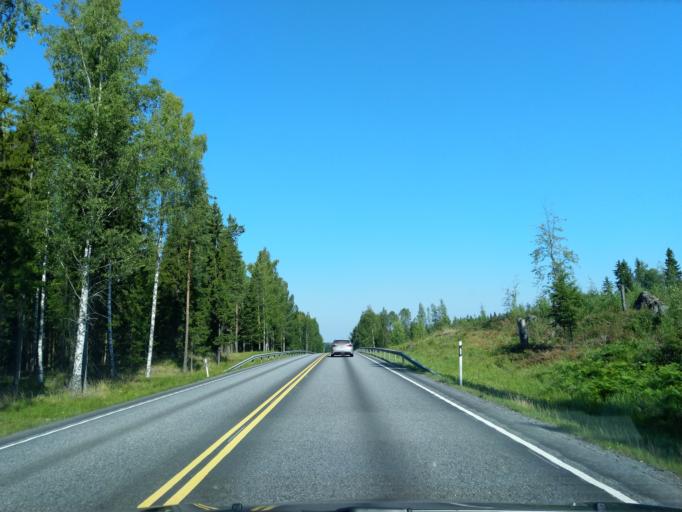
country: FI
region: Varsinais-Suomi
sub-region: Loimaa
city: Alastaro
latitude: 61.0801
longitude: 22.9042
